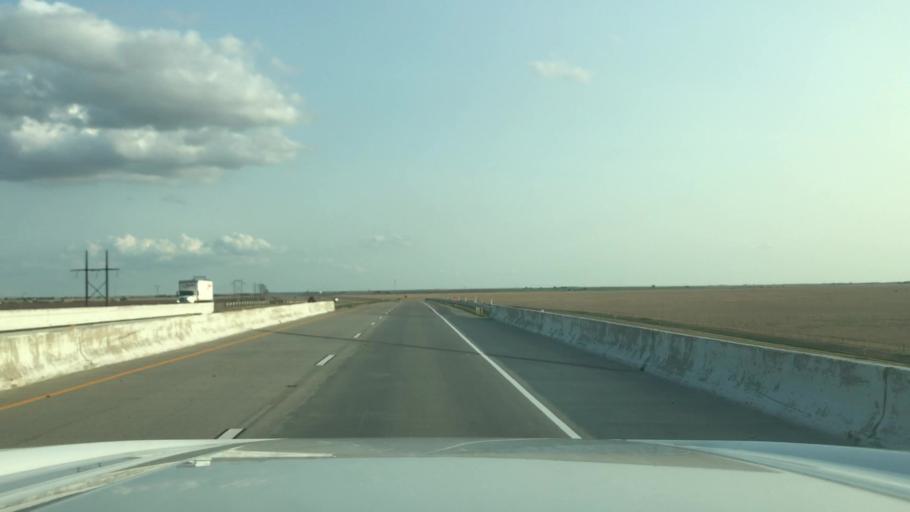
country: US
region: Texas
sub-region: Swisher County
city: Tulia
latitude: 34.5741
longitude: -101.7942
